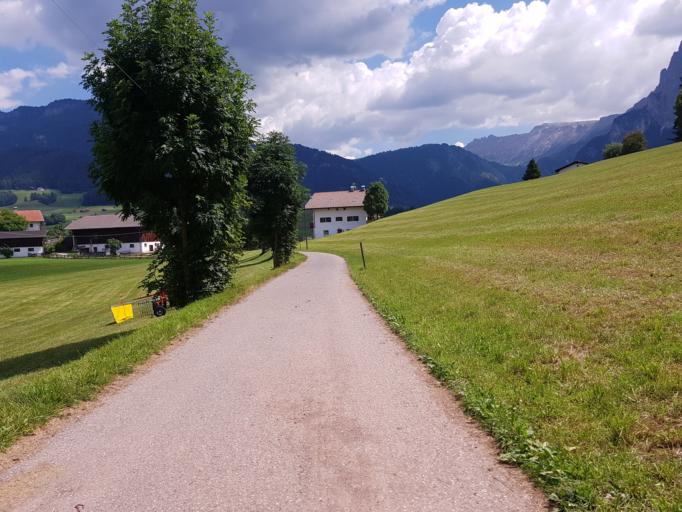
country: IT
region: Trentino-Alto Adige
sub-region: Bolzano
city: Castelrotto
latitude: 46.5601
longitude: 11.5466
